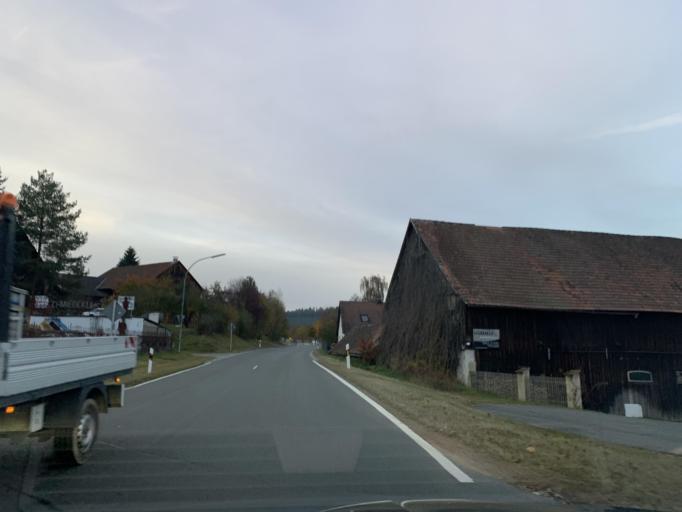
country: DE
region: Bavaria
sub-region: Upper Palatinate
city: Neunburg vorm Wald
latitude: 49.3698
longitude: 12.3792
